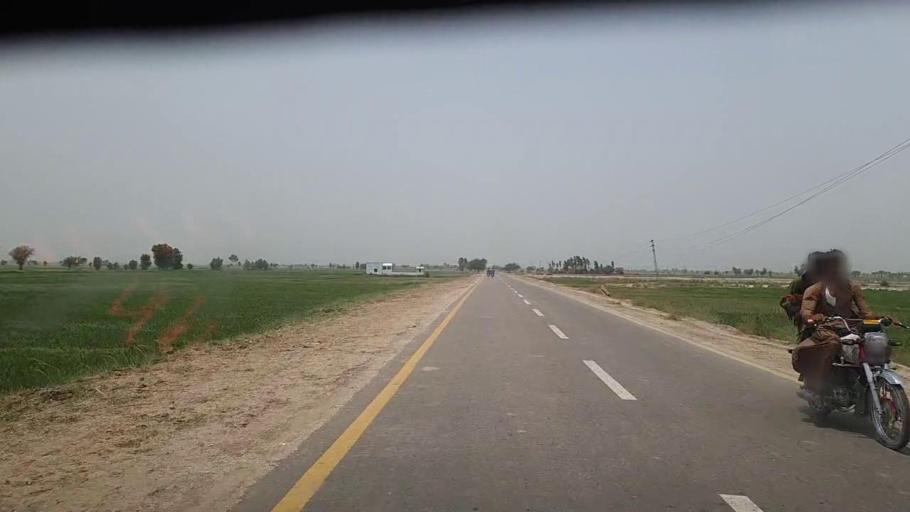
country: PK
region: Sindh
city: Sita Road
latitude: 27.0402
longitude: 67.8929
